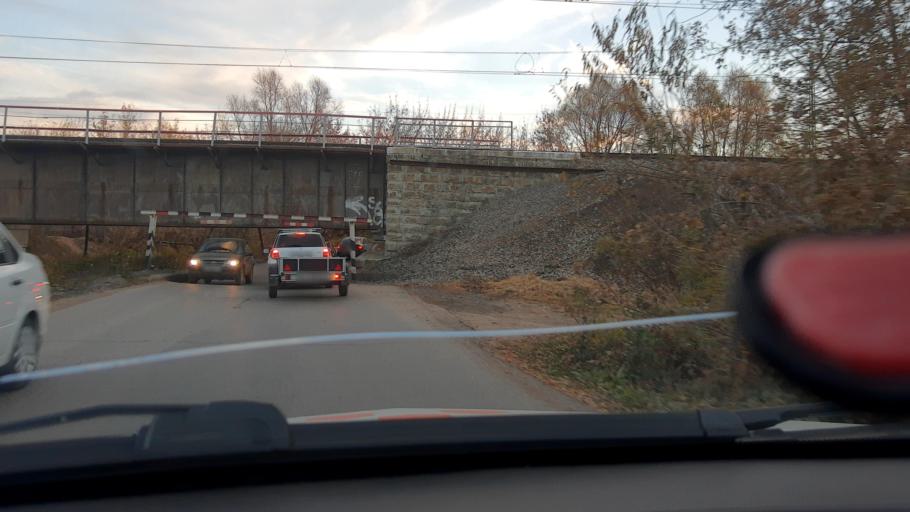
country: RU
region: Bashkortostan
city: Ufa
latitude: 54.8022
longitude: 56.1521
